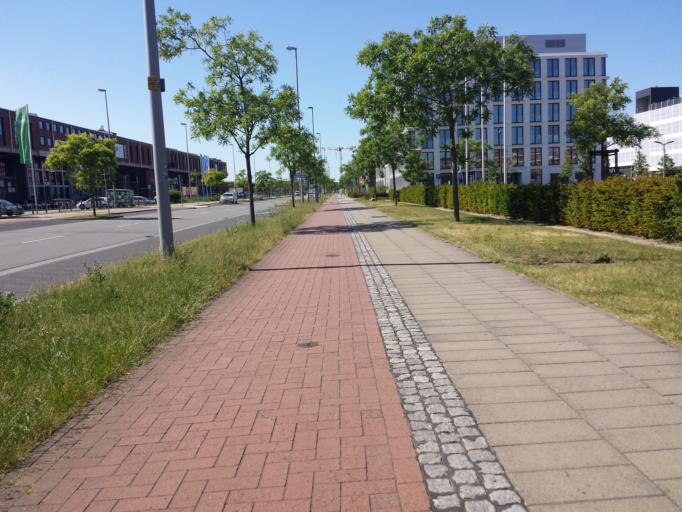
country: DE
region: Bremen
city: Bremen
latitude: 53.0903
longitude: 8.7764
